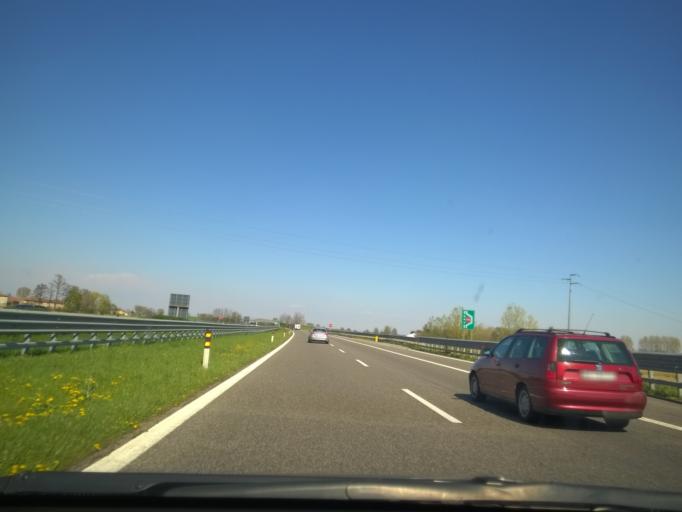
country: IT
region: Emilia-Romagna
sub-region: Provincia di Piacenza
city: Monticelli d'Ongina
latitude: 45.0661
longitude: 9.9551
